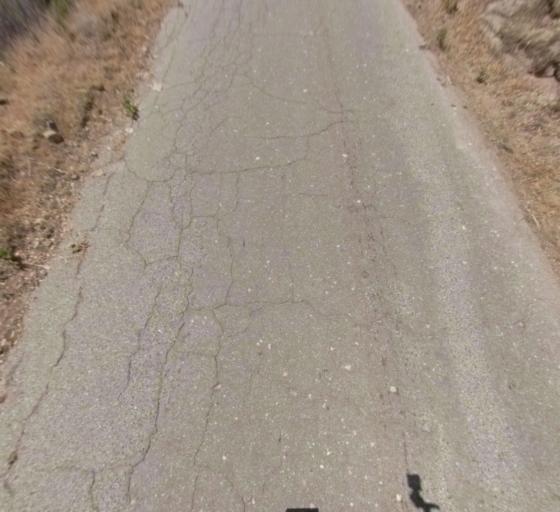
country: US
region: California
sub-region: Fresno County
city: Auberry
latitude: 37.1471
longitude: -119.4904
